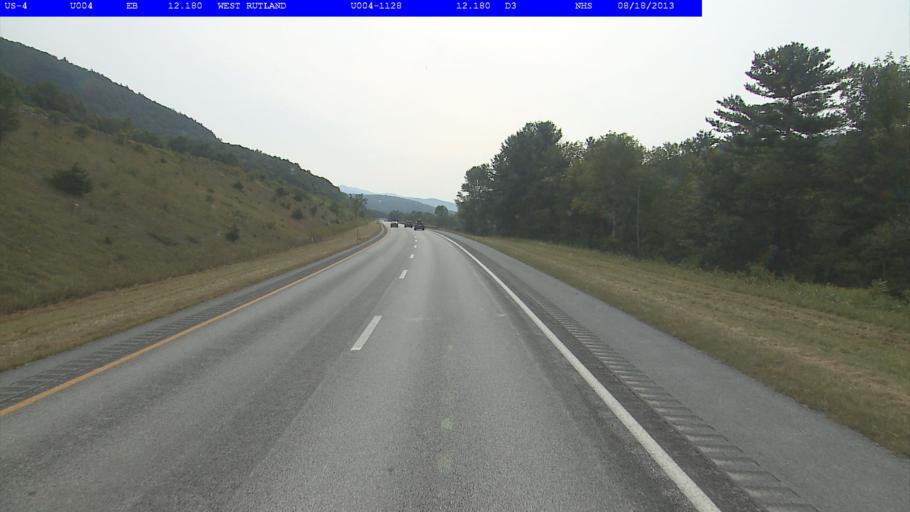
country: US
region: Vermont
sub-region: Rutland County
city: West Rutland
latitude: 43.6074
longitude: -73.0820
